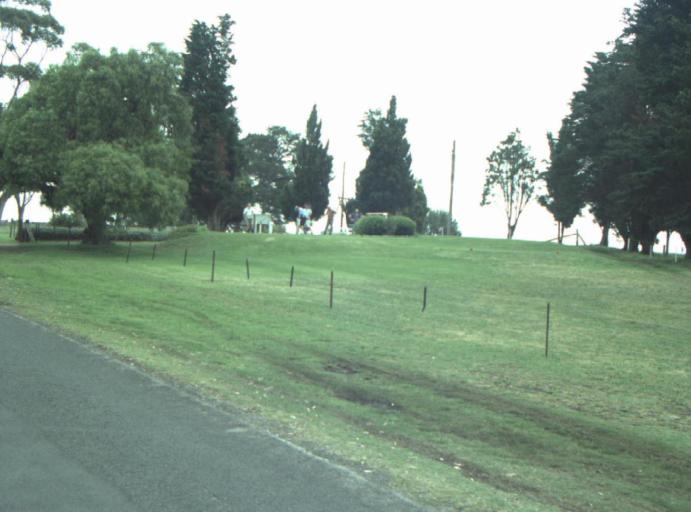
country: AU
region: Victoria
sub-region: Greater Geelong
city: East Geelong
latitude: -38.1474
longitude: 144.3858
